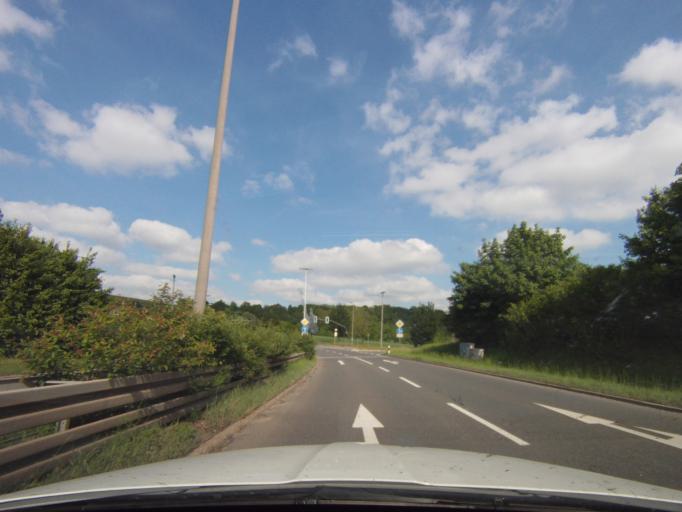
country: DE
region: Thuringia
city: Gera
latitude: 50.8617
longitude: 12.1089
